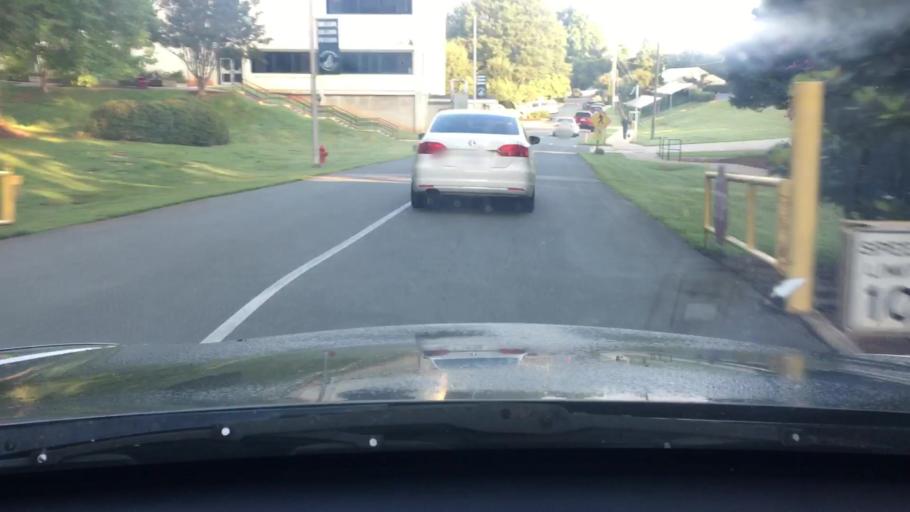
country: US
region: North Carolina
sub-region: Alamance County
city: Haw River
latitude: 36.0669
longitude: -79.3562
